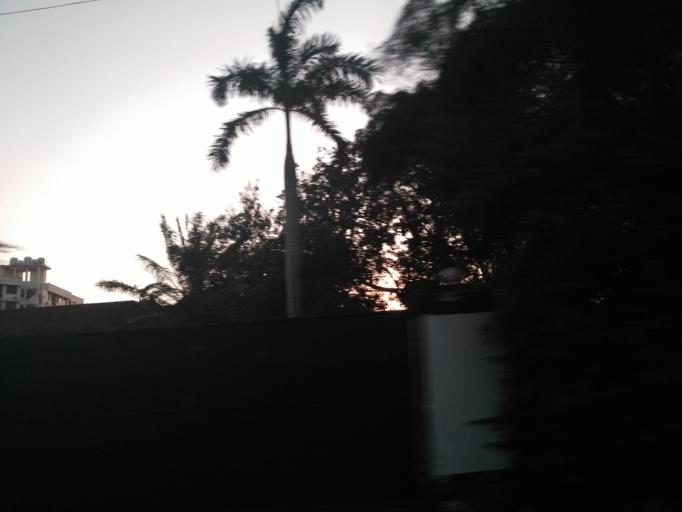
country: TZ
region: Dar es Salaam
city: Magomeni
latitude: -6.7698
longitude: 39.2769
